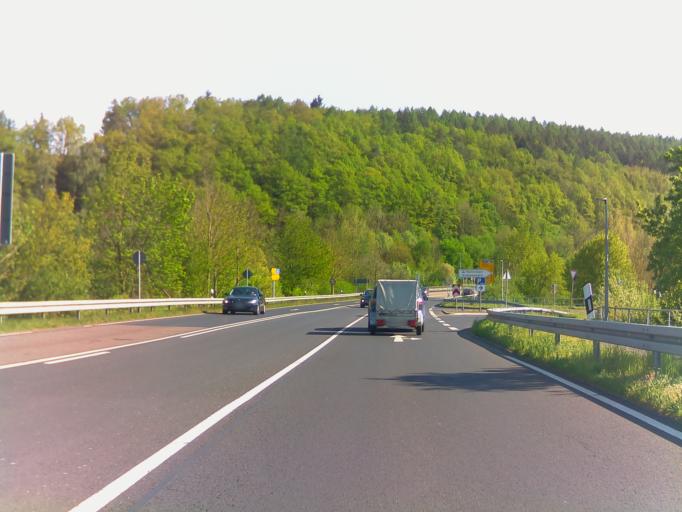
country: DE
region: Hesse
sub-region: Regierungsbezirk Darmstadt
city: Wachtersbach
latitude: 50.2553
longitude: 9.3011
